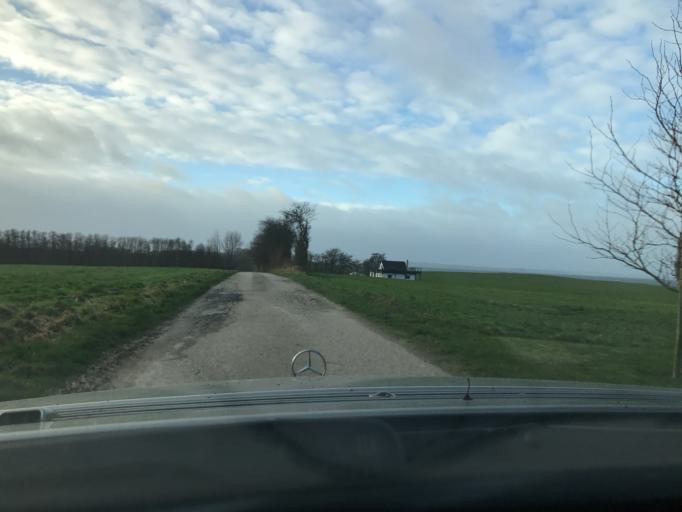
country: DK
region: South Denmark
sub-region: Sonderborg Kommune
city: Nordborg
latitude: 55.0518
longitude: 9.6540
